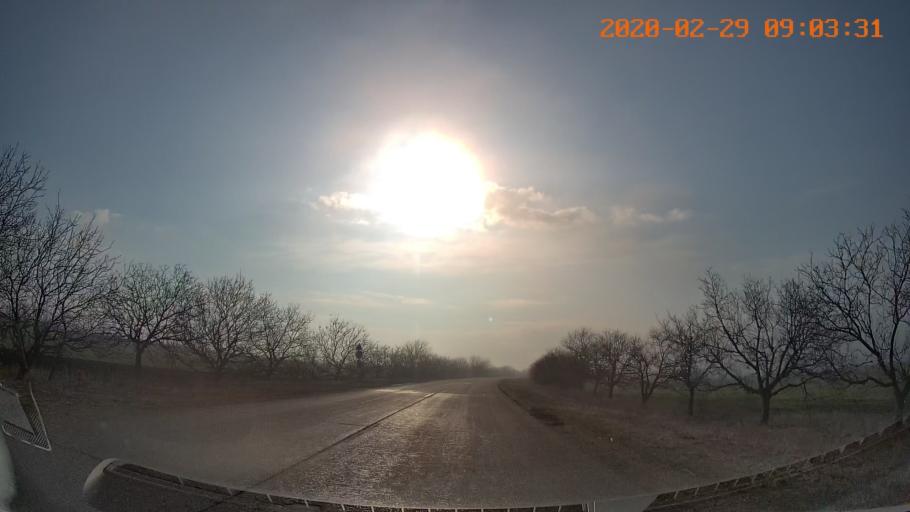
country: UA
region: Odessa
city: Velykoploske
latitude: 46.9151
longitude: 29.7298
